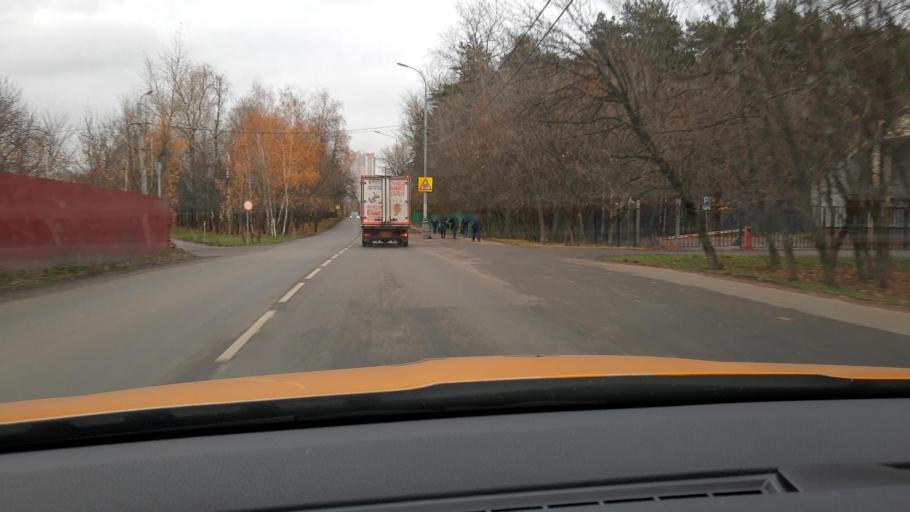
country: RU
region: Moskovskaya
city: Shcherbinka
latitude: 55.5426
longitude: 37.5744
